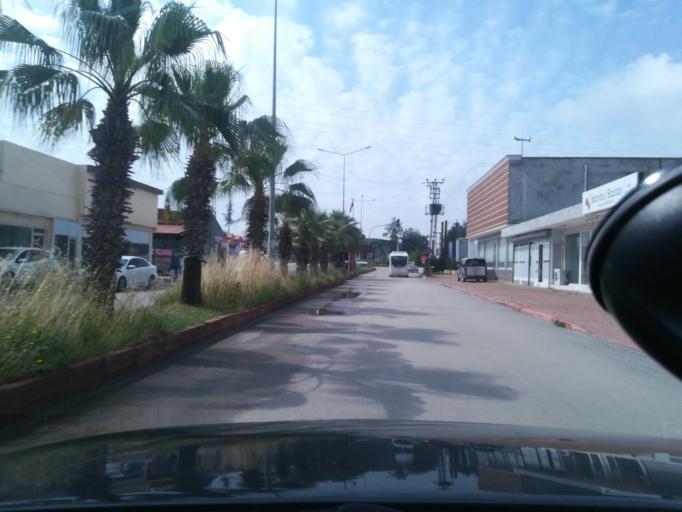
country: TR
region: Adana
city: Yuregir
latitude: 36.9832
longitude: 35.4304
